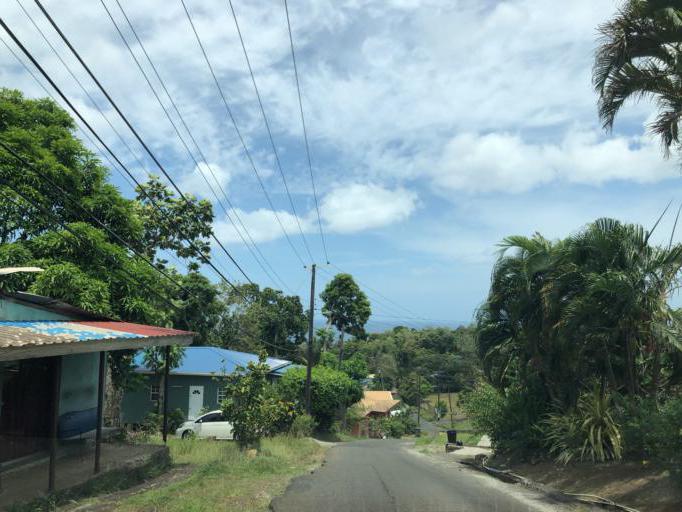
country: LC
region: Castries Quarter
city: Castries
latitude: 13.9929
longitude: -61.0081
